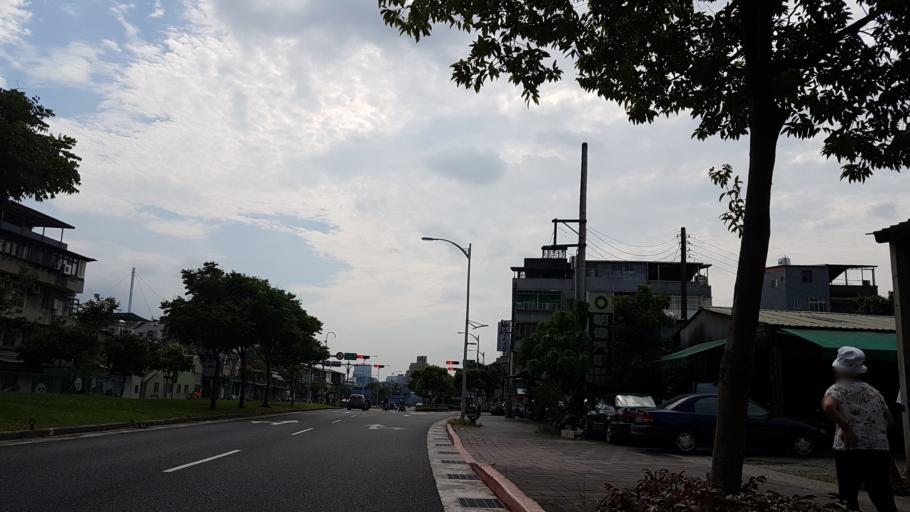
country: TW
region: Taipei
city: Taipei
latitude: 25.0542
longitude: 121.6142
